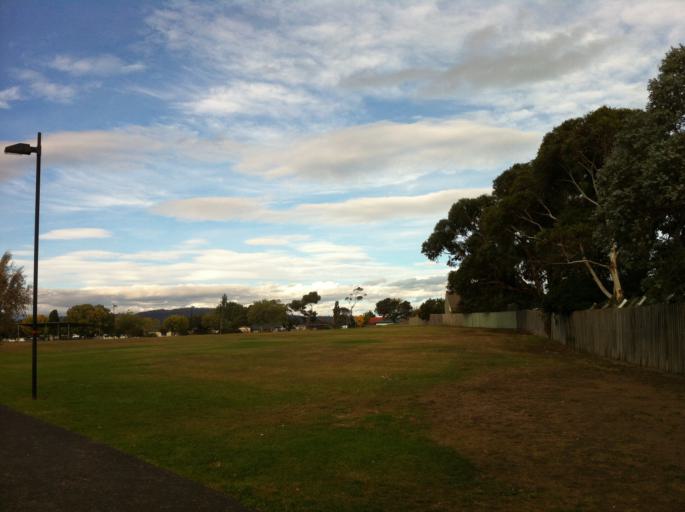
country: AU
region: Tasmania
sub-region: Glenorchy
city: Moonah
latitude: -42.8466
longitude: 147.2999
